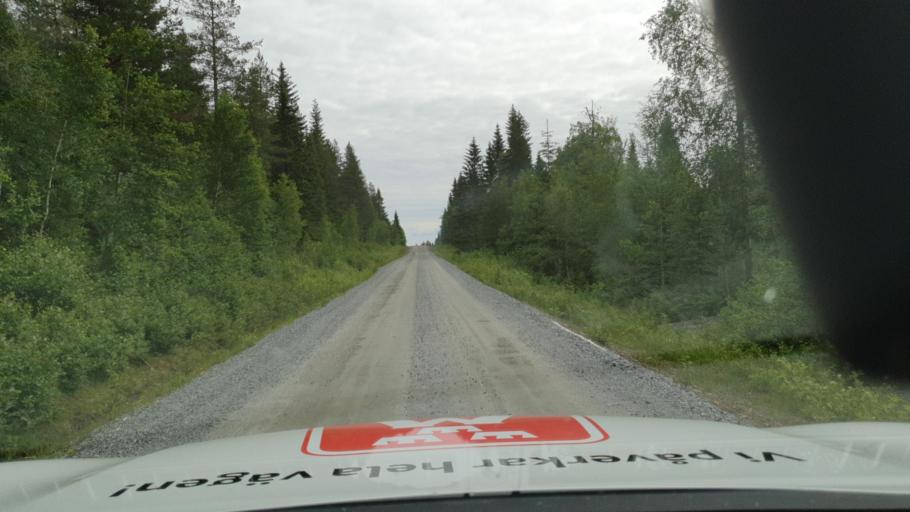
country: SE
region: Vaesterbotten
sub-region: Skelleftea Kommun
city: Langsele
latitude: 64.6480
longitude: 20.3027
